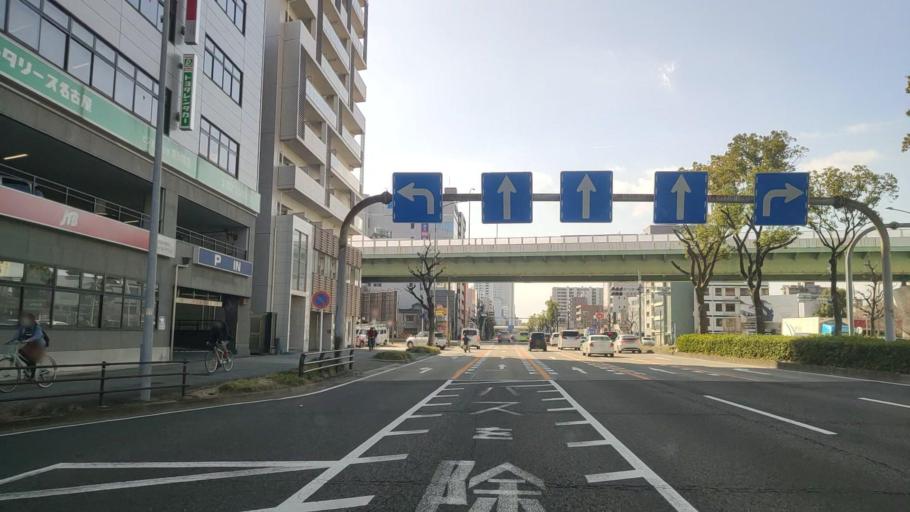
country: JP
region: Aichi
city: Nagoya-shi
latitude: 35.1523
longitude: 136.8990
